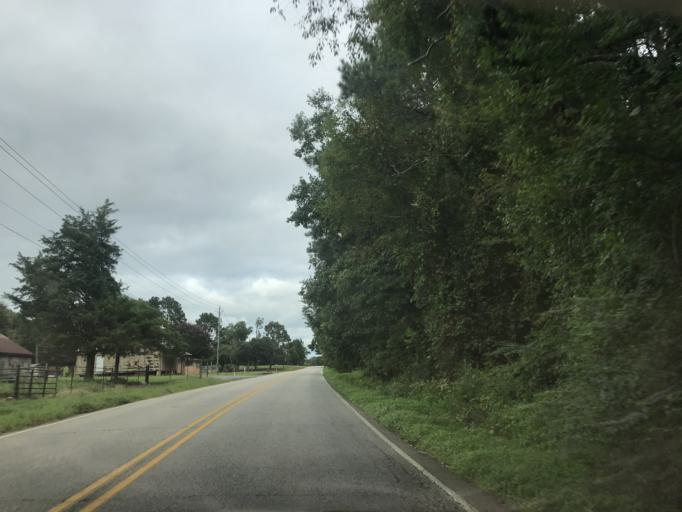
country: US
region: North Carolina
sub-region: Wake County
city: Garner
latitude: 35.5742
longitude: -78.5802
